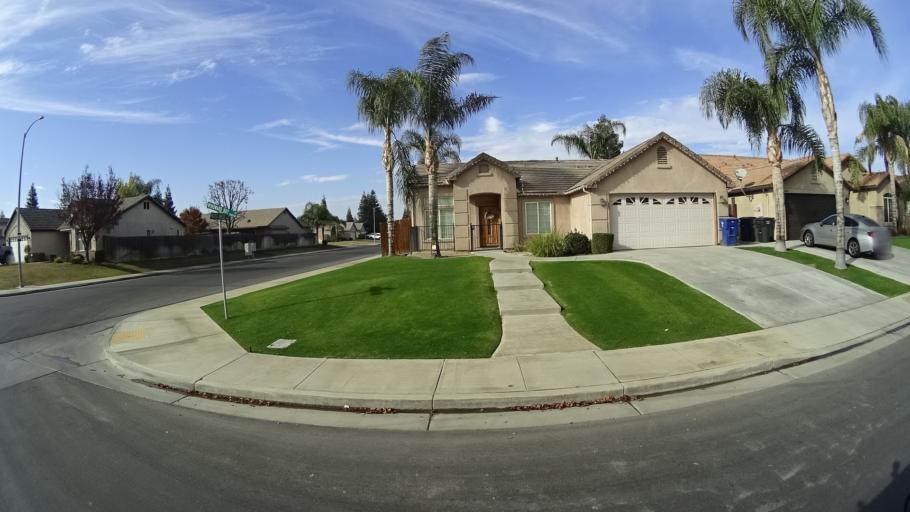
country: US
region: California
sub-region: Kern County
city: Rosedale
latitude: 35.4113
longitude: -119.1285
